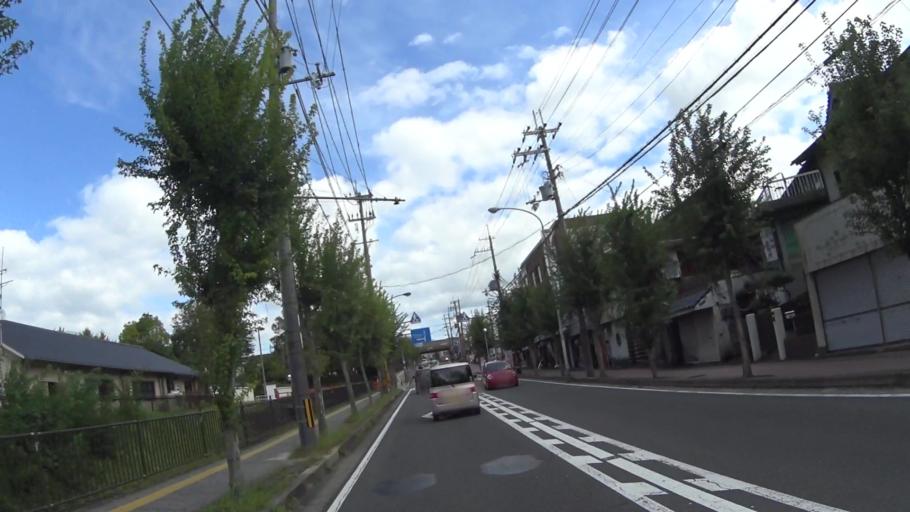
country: JP
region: Kyoto
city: Uji
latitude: 34.8738
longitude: 135.7744
